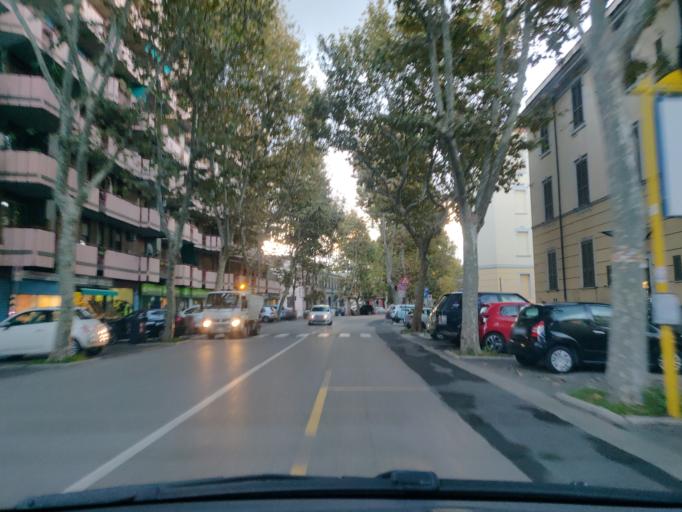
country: IT
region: Latium
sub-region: Citta metropolitana di Roma Capitale
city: Civitavecchia
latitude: 42.0906
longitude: 11.8023
